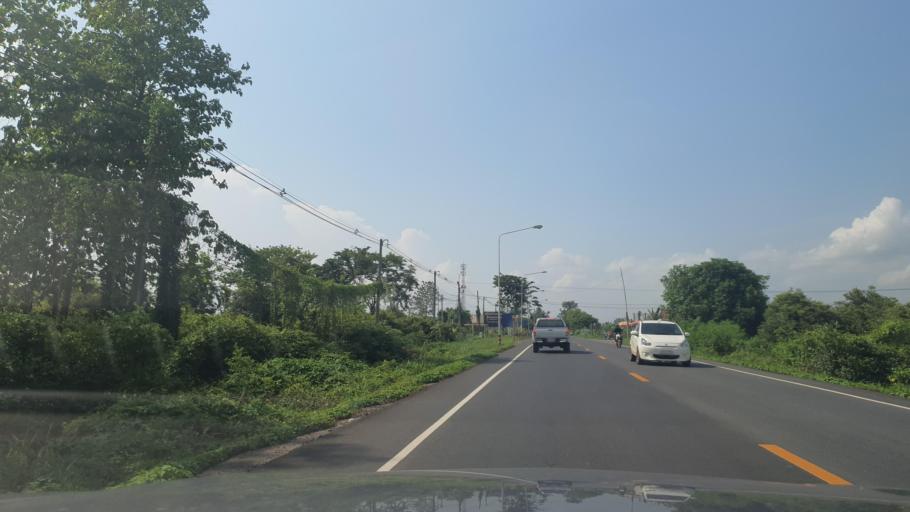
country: TH
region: Sukhothai
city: Si Samrong
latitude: 17.2129
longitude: 99.8496
